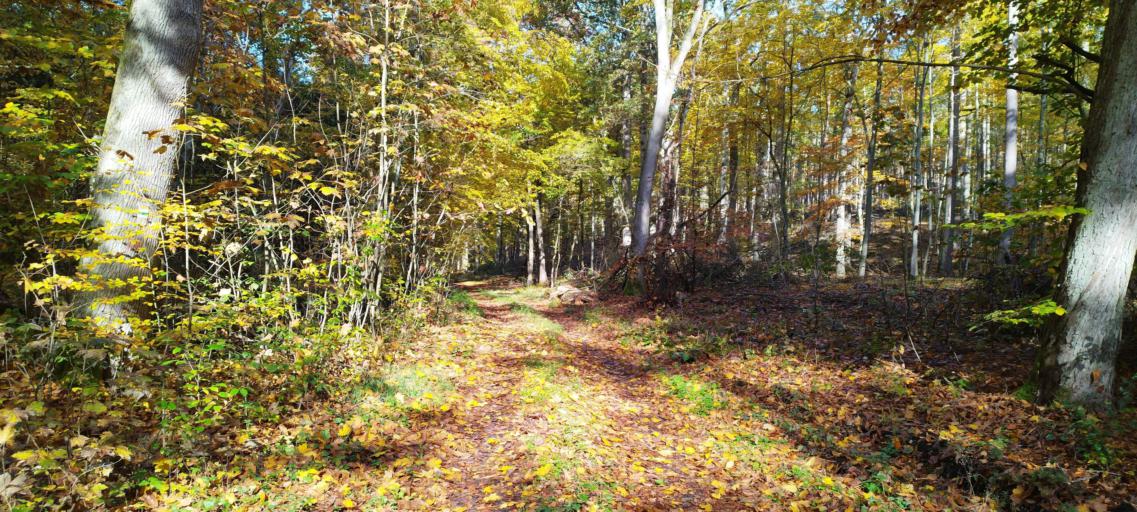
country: DE
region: Brandenburg
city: Strausberg
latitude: 52.6174
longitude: 13.8981
